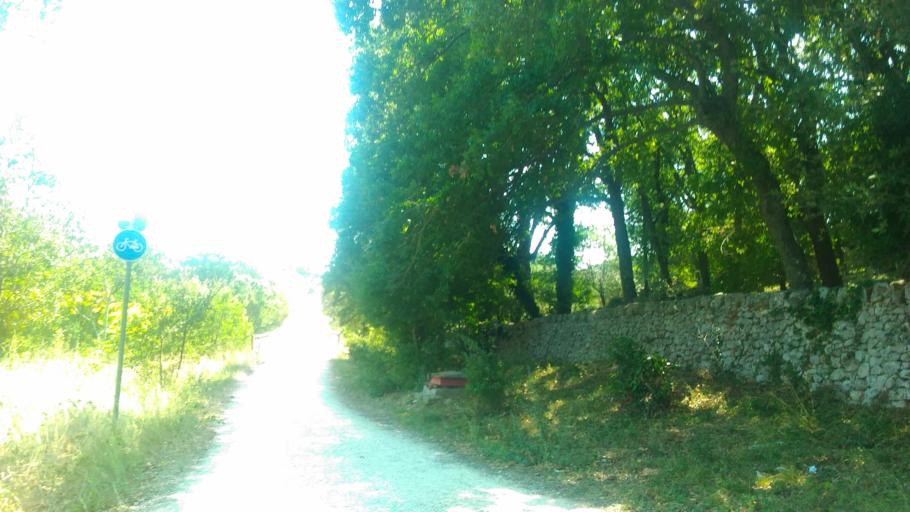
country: IT
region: Apulia
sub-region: Provincia di Brindisi
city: Cisternino
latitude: 40.7304
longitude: 17.3909
